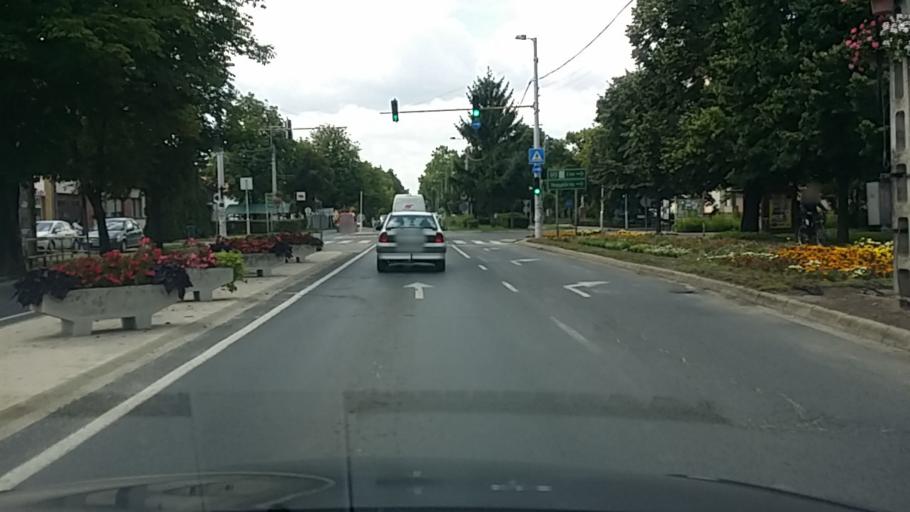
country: HU
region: Bacs-Kiskun
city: Lajosmizse
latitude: 47.0260
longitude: 19.5581
